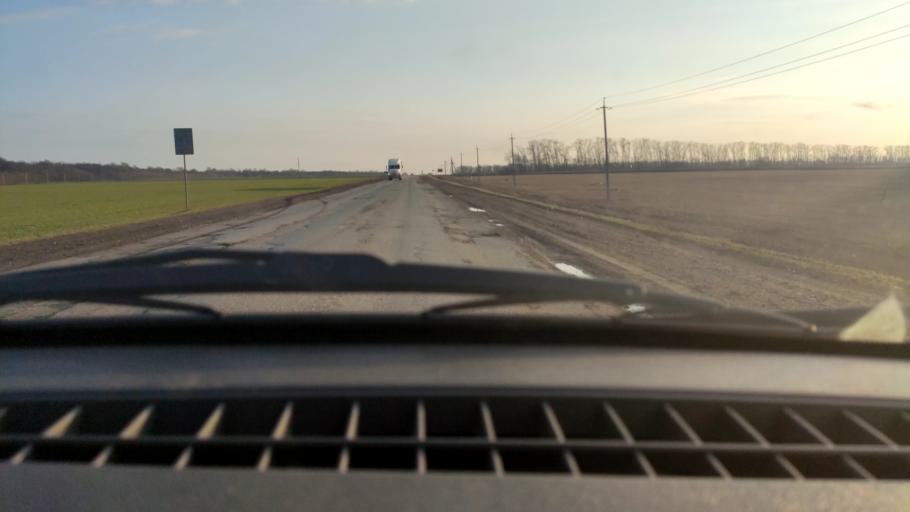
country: RU
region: Bashkortostan
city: Chishmy
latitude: 54.5661
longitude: 55.3490
